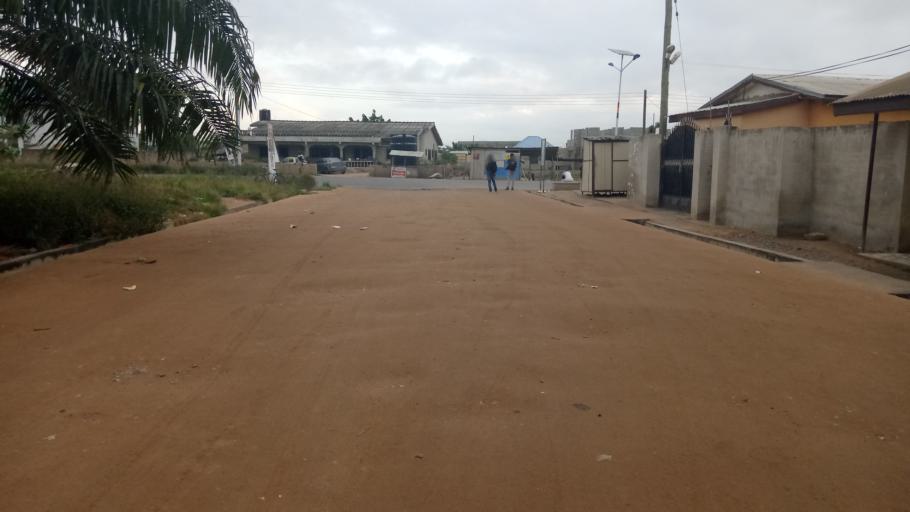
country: GH
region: Central
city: Kasoa
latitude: 5.5027
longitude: -0.4102
